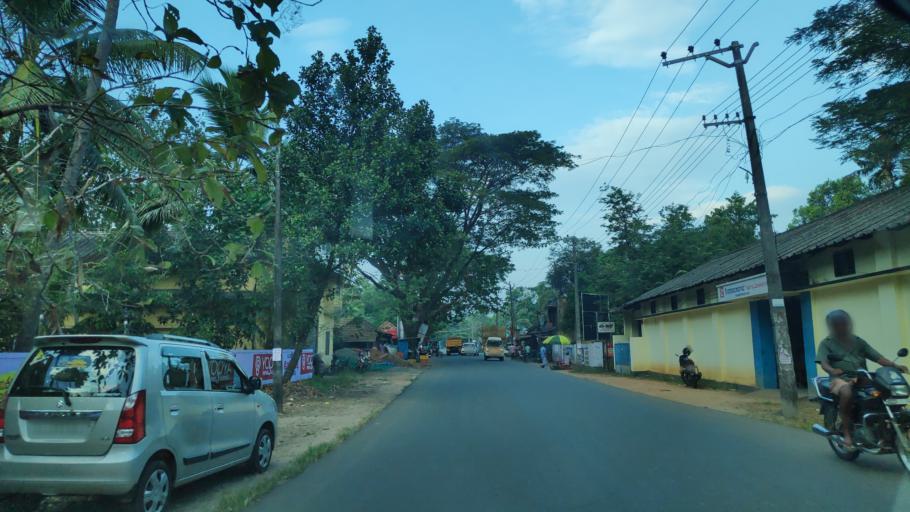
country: IN
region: Kerala
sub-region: Alappuzha
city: Shertallai
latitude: 9.6518
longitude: 76.3740
